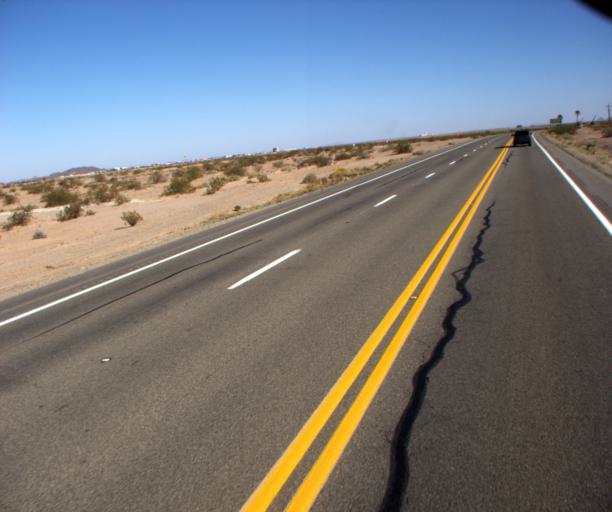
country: US
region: Arizona
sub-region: Yuma County
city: Fortuna Foothills
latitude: 32.8168
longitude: -114.3790
